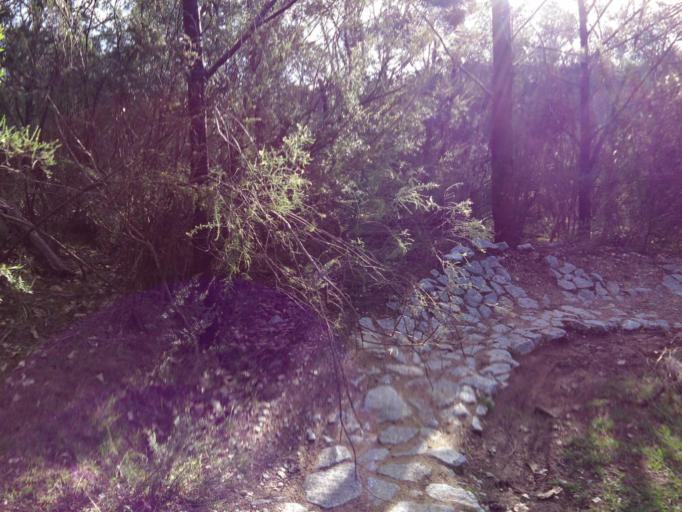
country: AU
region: Victoria
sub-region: Yarra Ranges
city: Lysterfield
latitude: -37.9445
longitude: 145.2749
